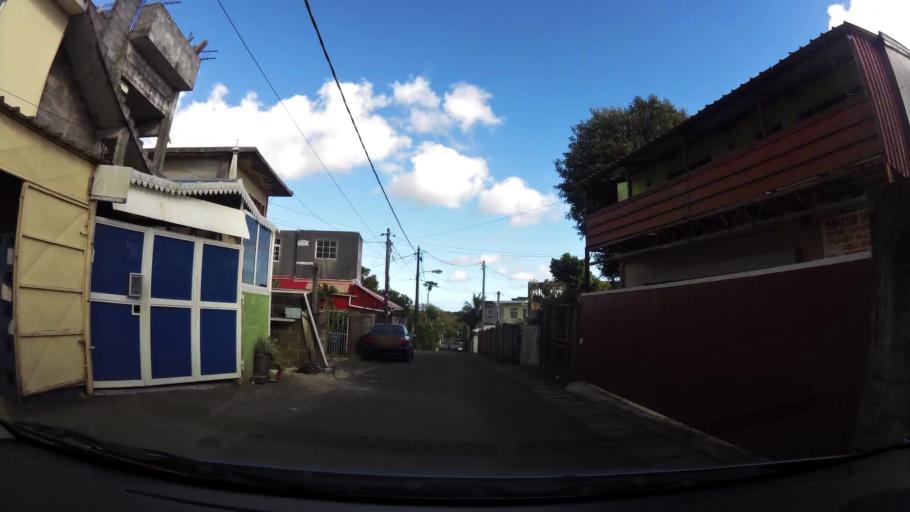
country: MU
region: Plaines Wilhems
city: Curepipe
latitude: -20.3011
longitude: 57.5142
